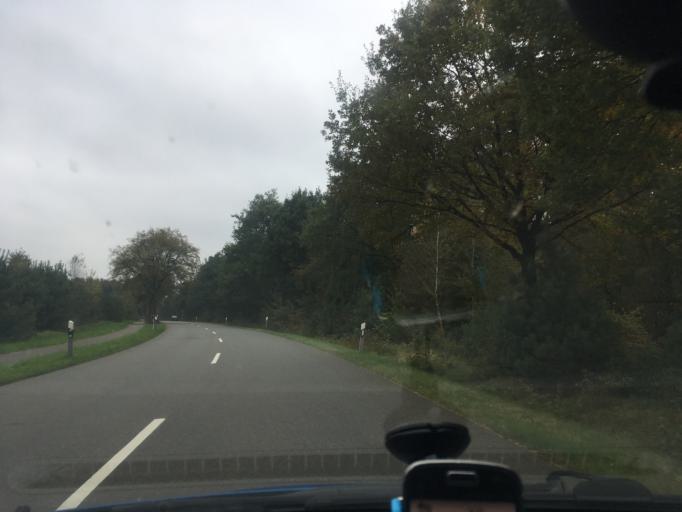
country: DE
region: Lower Saxony
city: Soderstorf
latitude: 53.1257
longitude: 10.1066
